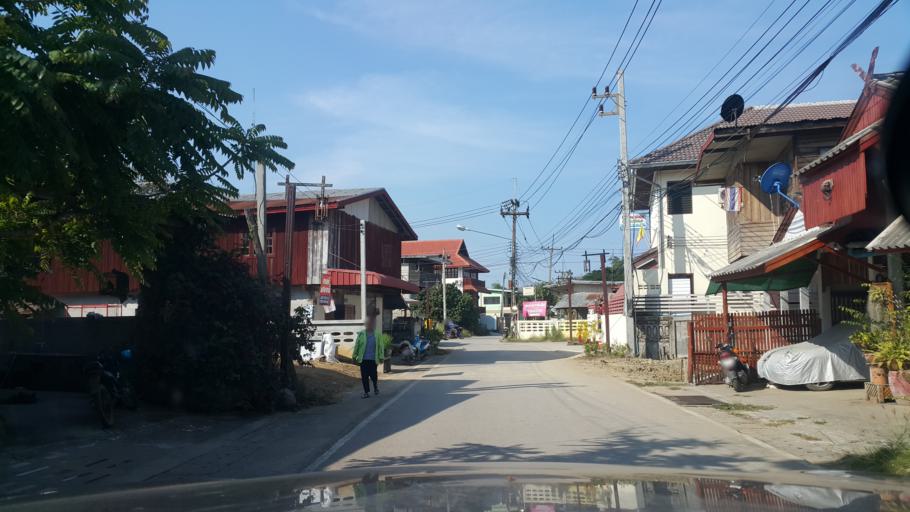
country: TH
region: Loei
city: Chiang Khan
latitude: 17.8922
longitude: 101.6474
